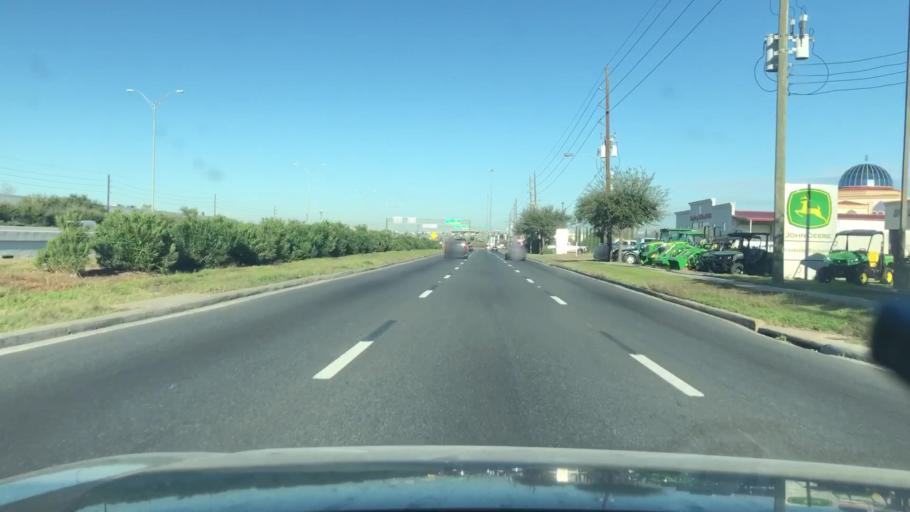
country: US
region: Texas
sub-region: Fort Bend County
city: Missouri City
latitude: 29.6498
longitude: -95.5452
